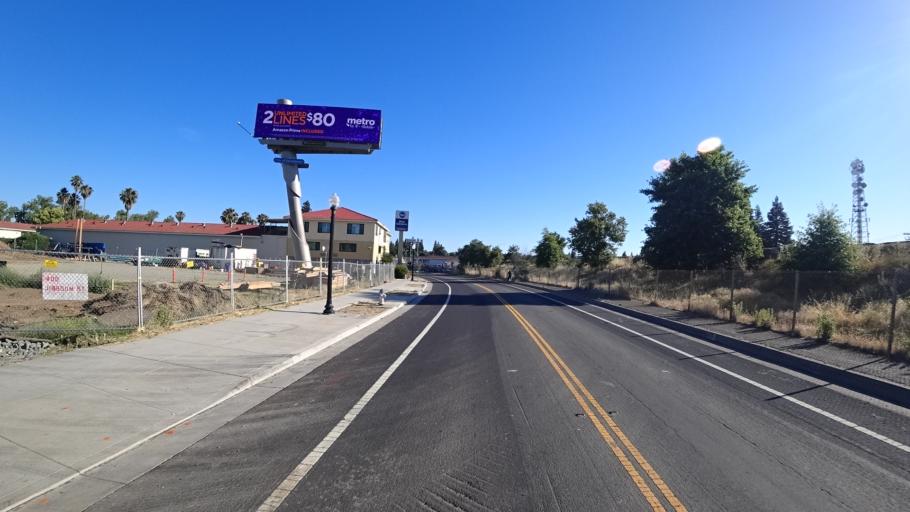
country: US
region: California
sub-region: Sacramento County
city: Sacramento
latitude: 38.5938
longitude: -121.5049
